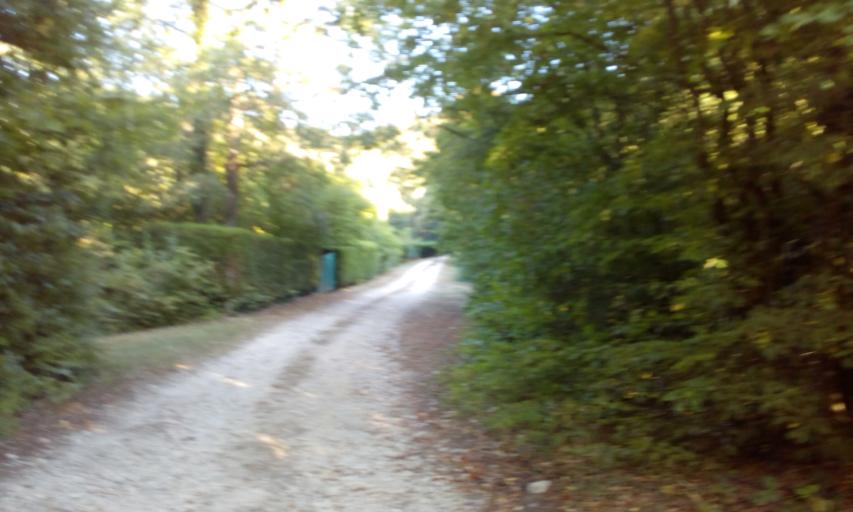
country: FR
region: Lorraine
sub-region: Departement de Meurthe-et-Moselle
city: Pagny-sur-Moselle
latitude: 48.9649
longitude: 5.8827
